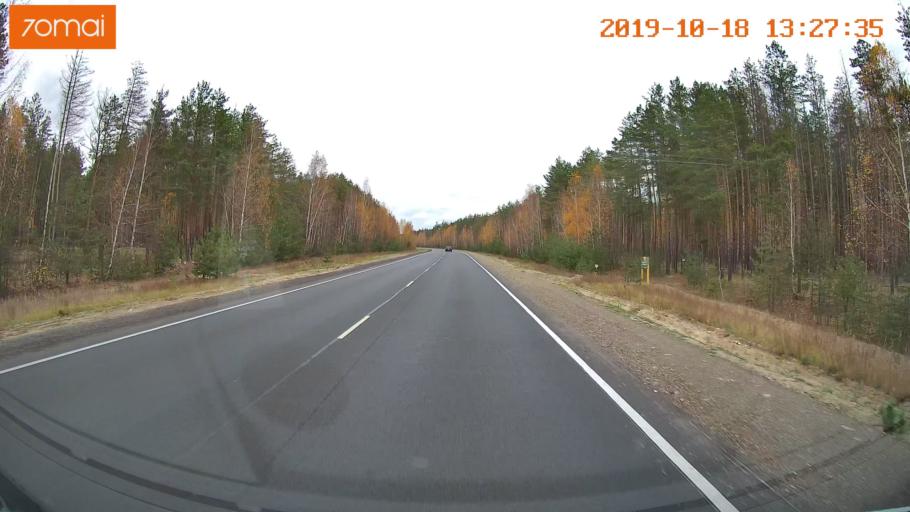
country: RU
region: Rjazan
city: Solotcha
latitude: 54.7658
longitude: 39.8568
